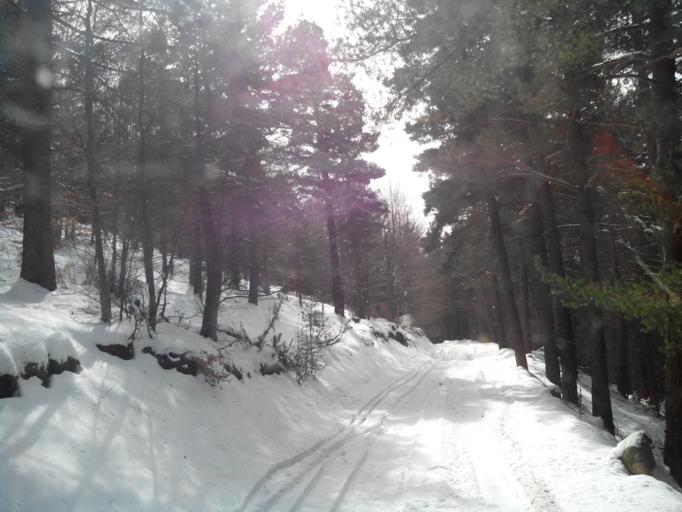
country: ES
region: Catalonia
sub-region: Provincia de Barcelona
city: Sant Julia de Cerdanyola
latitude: 42.1996
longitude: 1.9299
